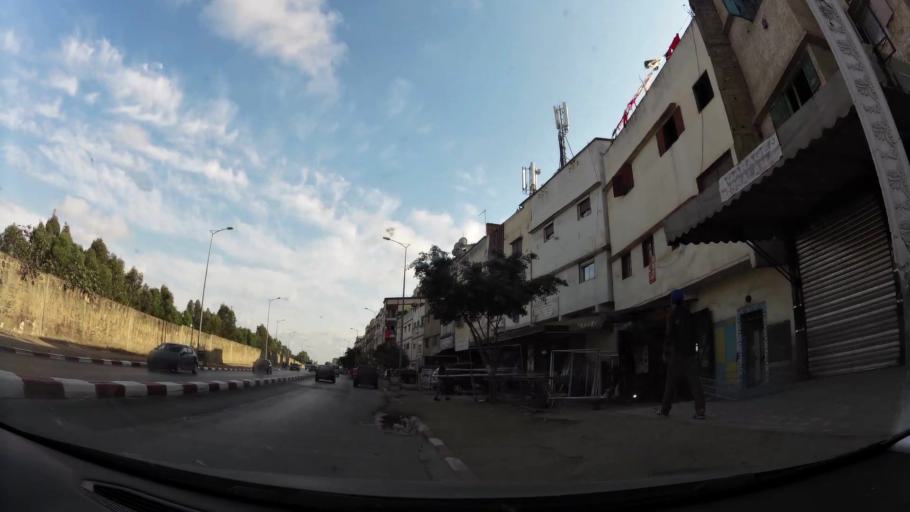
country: MA
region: Rabat-Sale-Zemmour-Zaer
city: Sale
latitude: 34.0526
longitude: -6.7736
